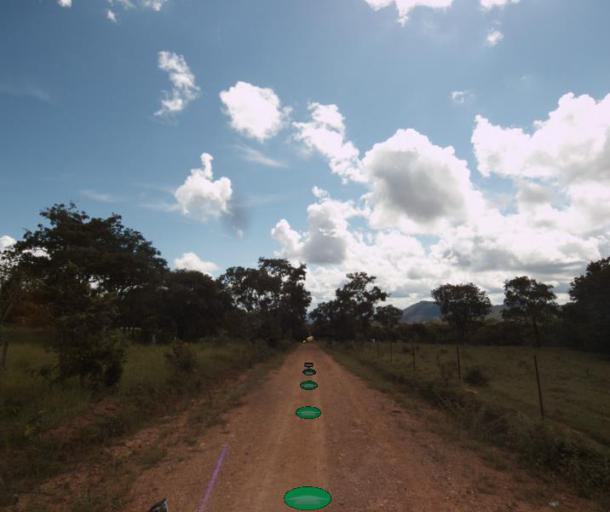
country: BR
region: Goias
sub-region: Pirenopolis
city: Pirenopolis
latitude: -15.7850
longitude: -48.9266
